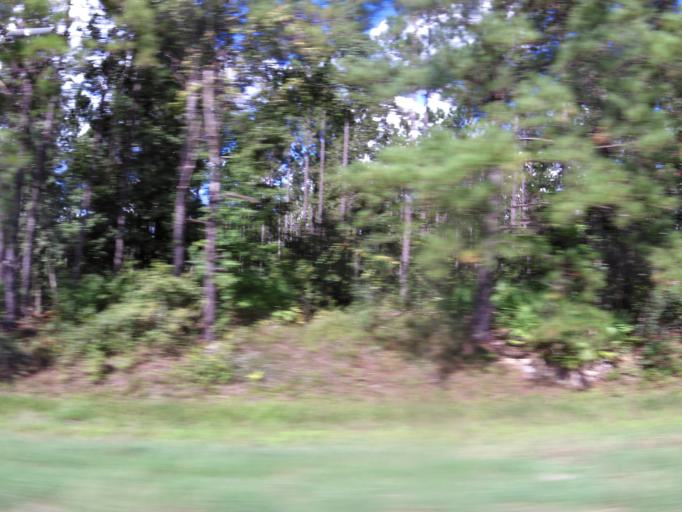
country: US
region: Georgia
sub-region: Lowndes County
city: Valdosta
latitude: 30.7953
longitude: -83.1871
